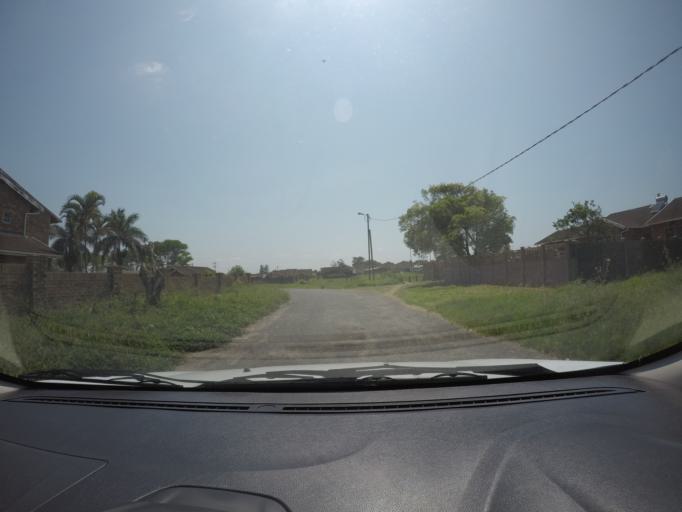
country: ZA
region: KwaZulu-Natal
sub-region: uThungulu District Municipality
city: eSikhawini
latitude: -28.8642
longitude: 31.9243
